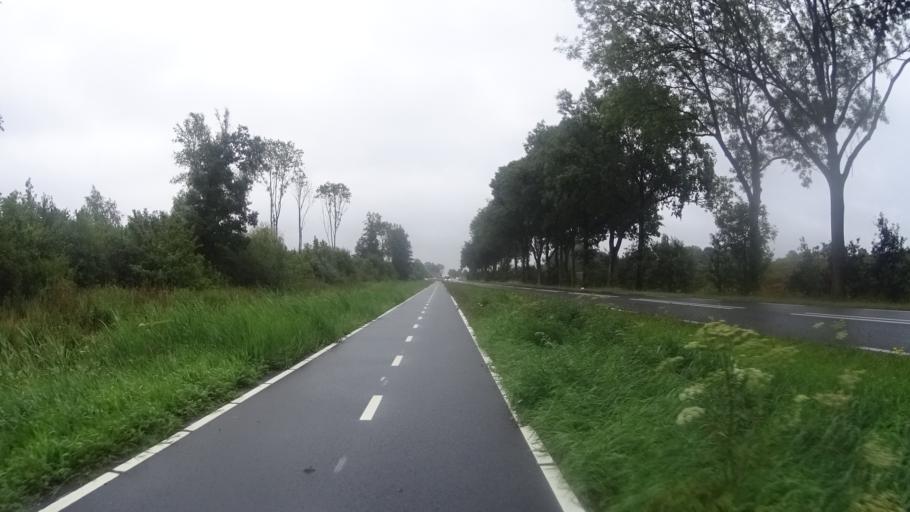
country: NL
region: Groningen
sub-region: Gemeente  Oldambt
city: Winschoten
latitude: 53.1631
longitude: 7.0122
